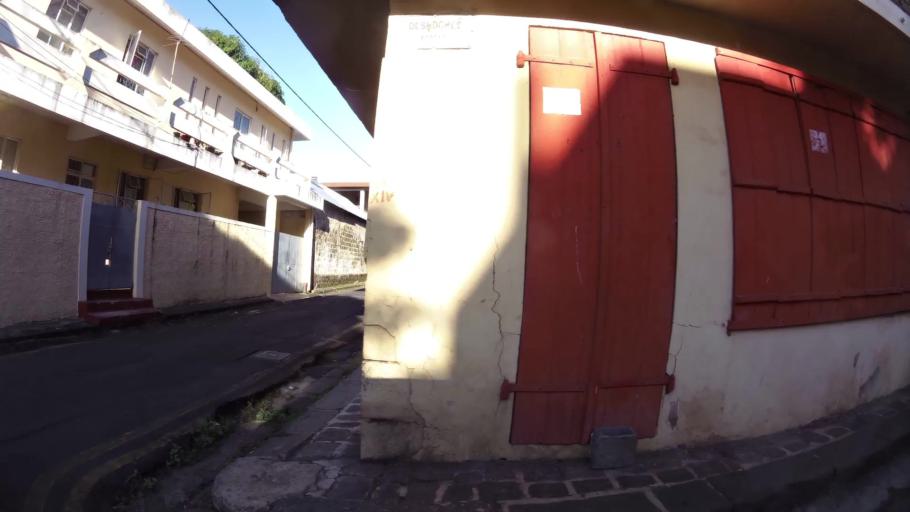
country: MU
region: Port Louis
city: Port Louis
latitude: -20.1673
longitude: 57.5012
